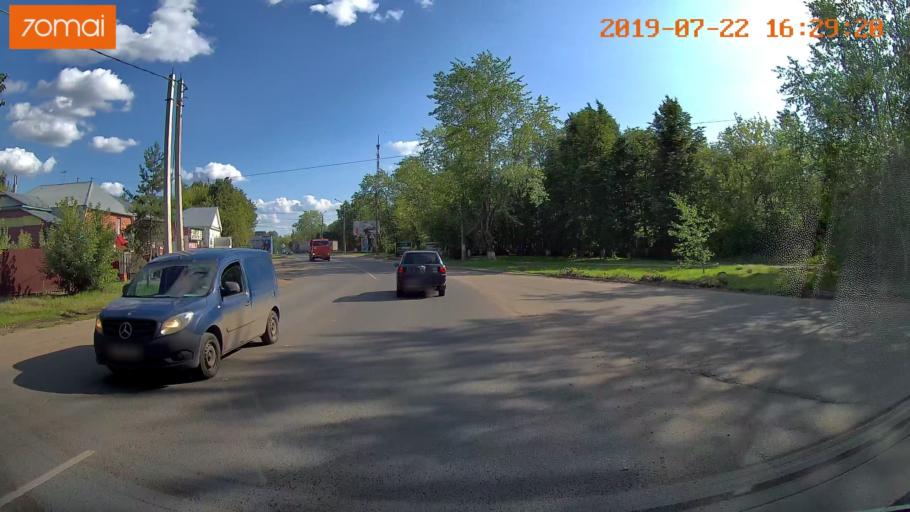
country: RU
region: Ivanovo
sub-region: Gorod Ivanovo
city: Ivanovo
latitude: 57.0320
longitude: 40.9480
